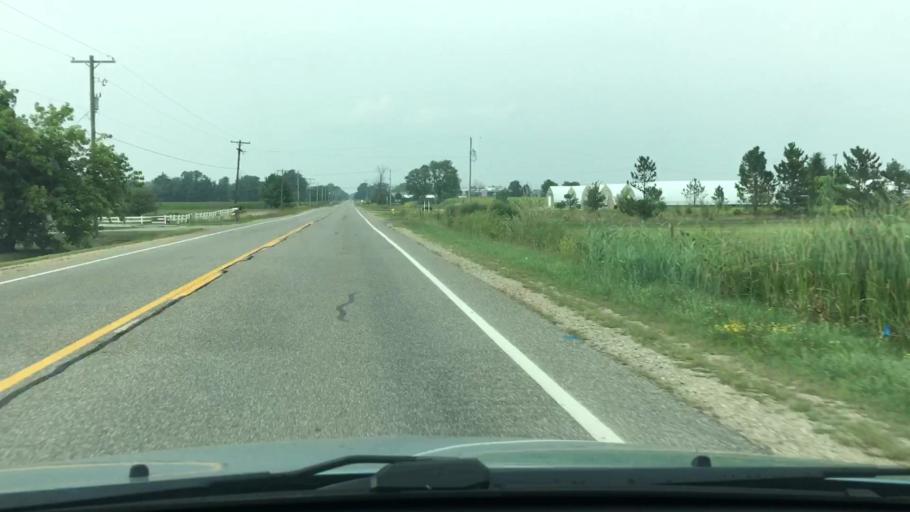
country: US
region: Michigan
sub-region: Ottawa County
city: Hudsonville
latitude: 42.8682
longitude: -85.9009
